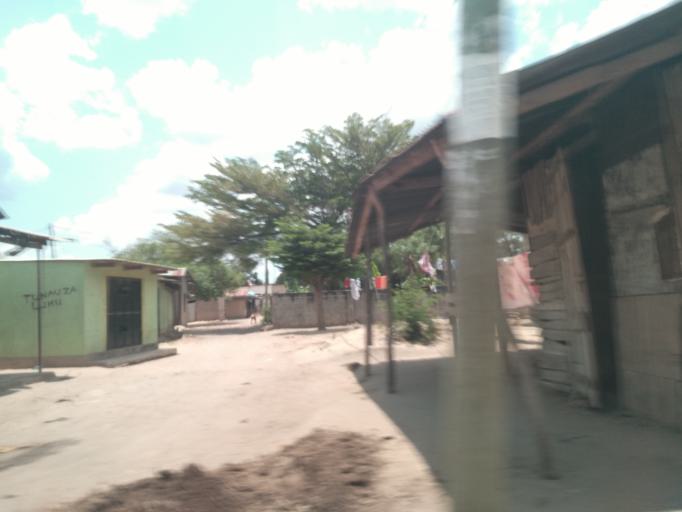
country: TZ
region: Dar es Salaam
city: Dar es Salaam
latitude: -6.8373
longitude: 39.3220
